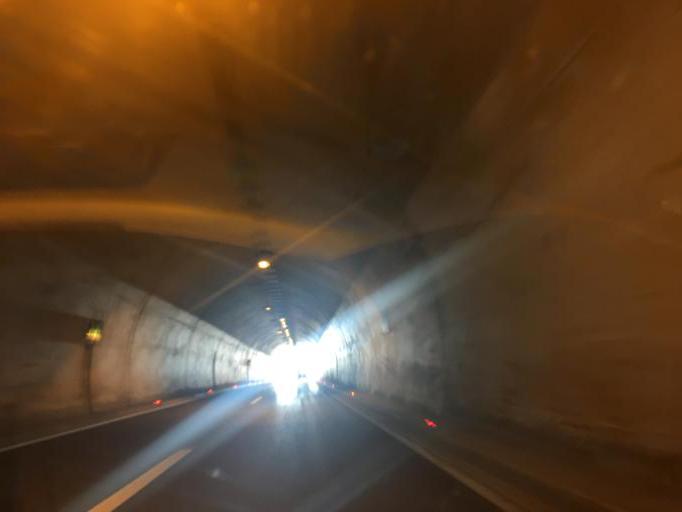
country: HR
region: Zadarska
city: Obrovac
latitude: 44.3651
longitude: 15.6382
